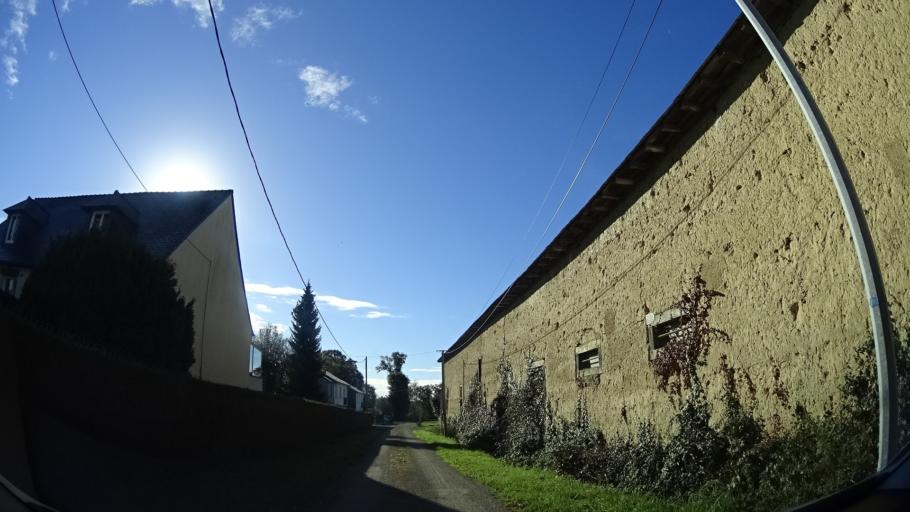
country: FR
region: Brittany
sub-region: Departement d'Ille-et-Vilaine
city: La Meziere
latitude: 48.2098
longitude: -1.7647
